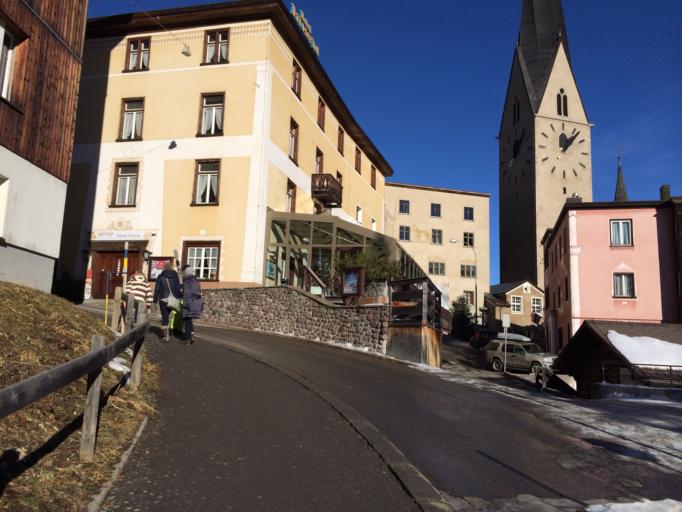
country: CH
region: Grisons
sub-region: Praettigau/Davos District
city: Davos
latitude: 46.7928
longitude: 9.8214
